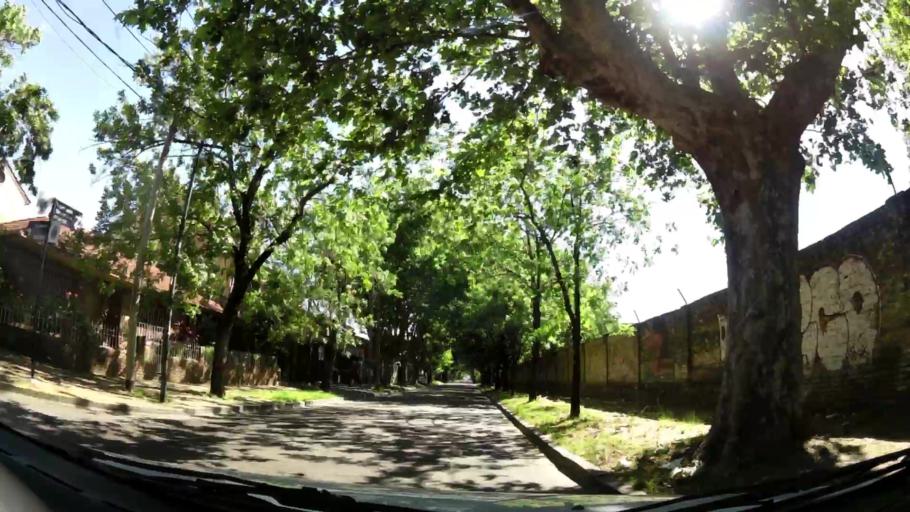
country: AR
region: Buenos Aires
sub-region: Partido de San Isidro
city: San Isidro
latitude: -34.4682
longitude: -58.5285
